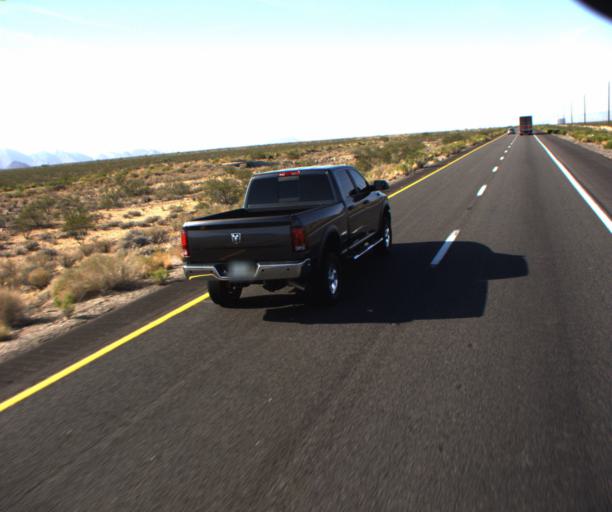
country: US
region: Arizona
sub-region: Mohave County
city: Kingman
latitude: 35.0755
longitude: -114.1230
